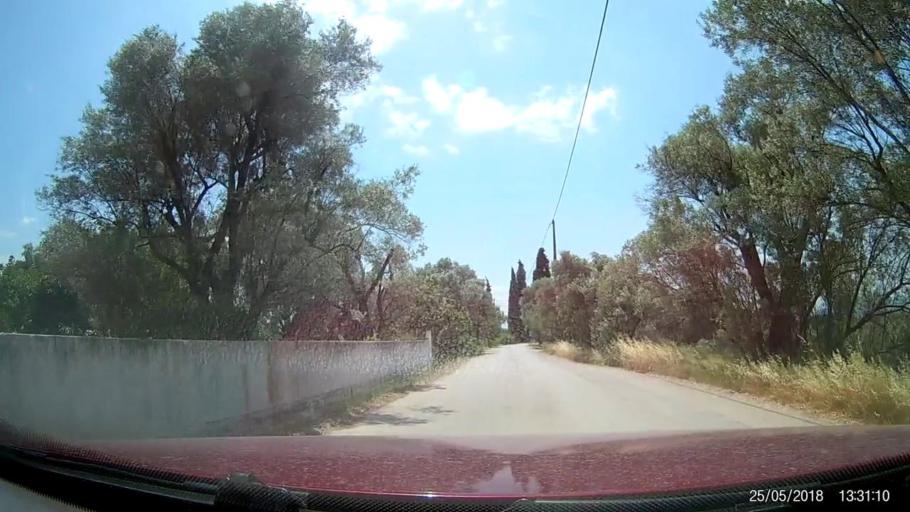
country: GR
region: Central Greece
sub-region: Nomos Evvoias
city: Mytikas
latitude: 38.4382
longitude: 23.6579
